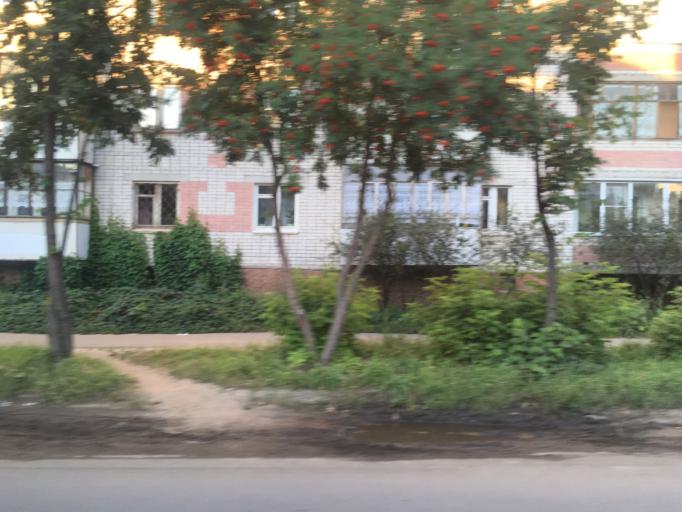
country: RU
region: Mariy-El
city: Yoshkar-Ola
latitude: 56.6473
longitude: 47.8646
